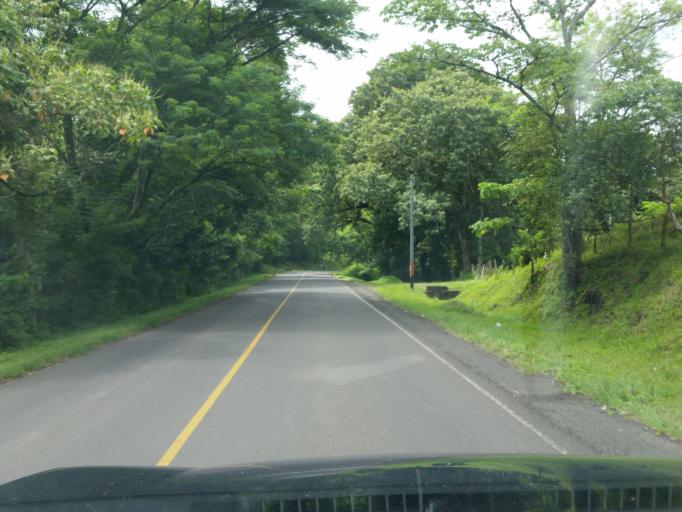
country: NI
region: Matagalpa
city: San Ramon
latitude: 13.1036
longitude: -85.7430
